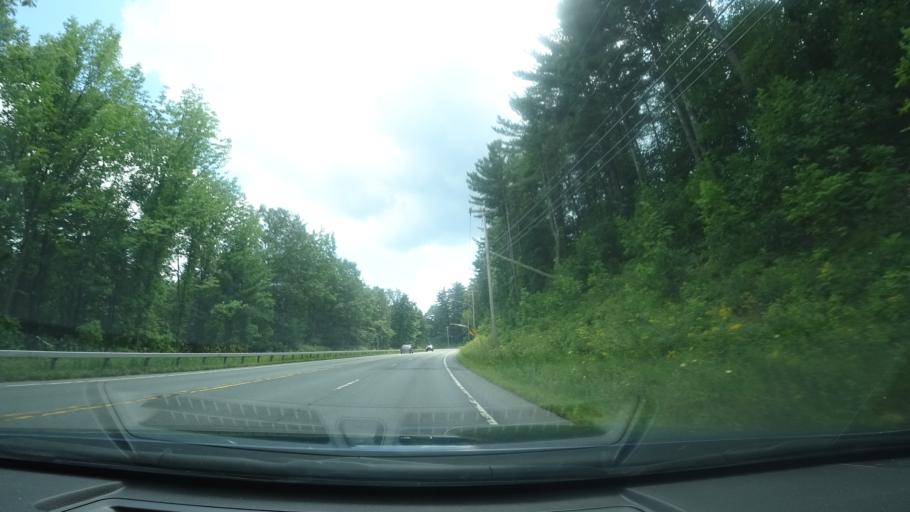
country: US
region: New York
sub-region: Warren County
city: Glens Falls North
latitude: 43.3998
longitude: -73.7051
